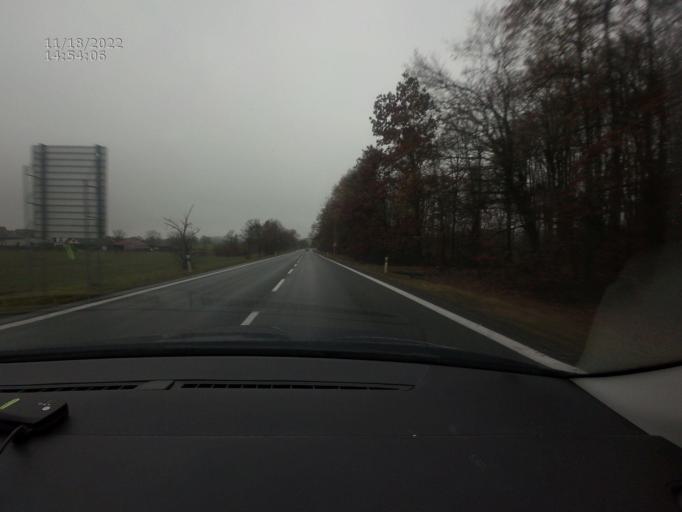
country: CZ
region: Jihocesky
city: Milevsko
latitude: 49.4606
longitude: 14.3361
